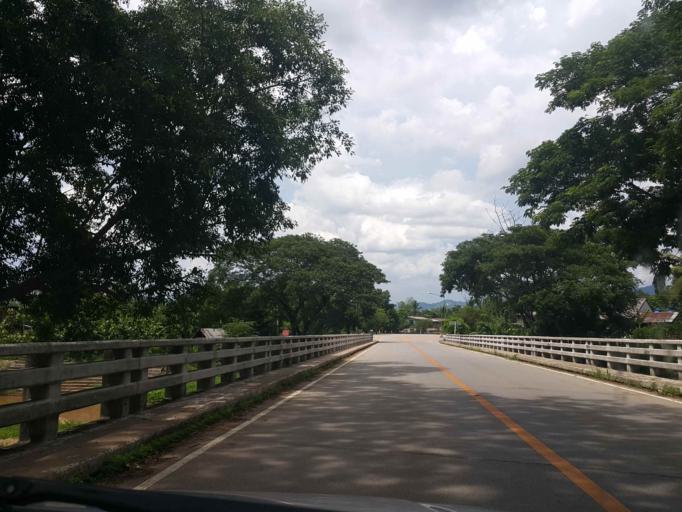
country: TH
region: Nan
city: Ban Luang
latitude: 18.8475
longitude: 100.4225
